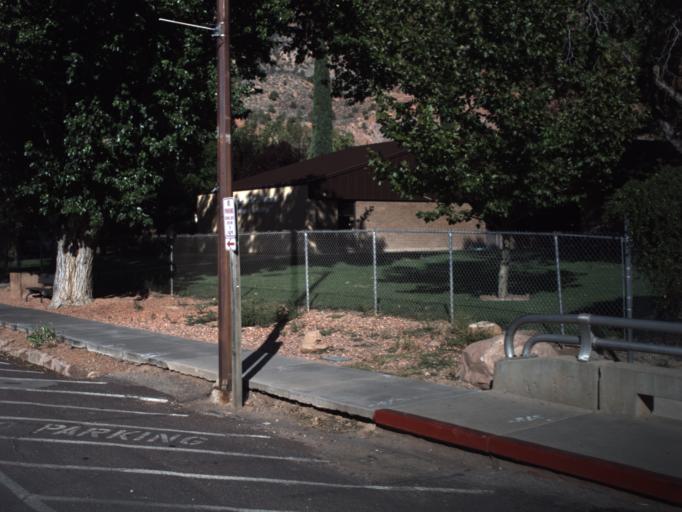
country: US
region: Utah
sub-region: Washington County
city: Hildale
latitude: 37.1889
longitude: -112.9988
